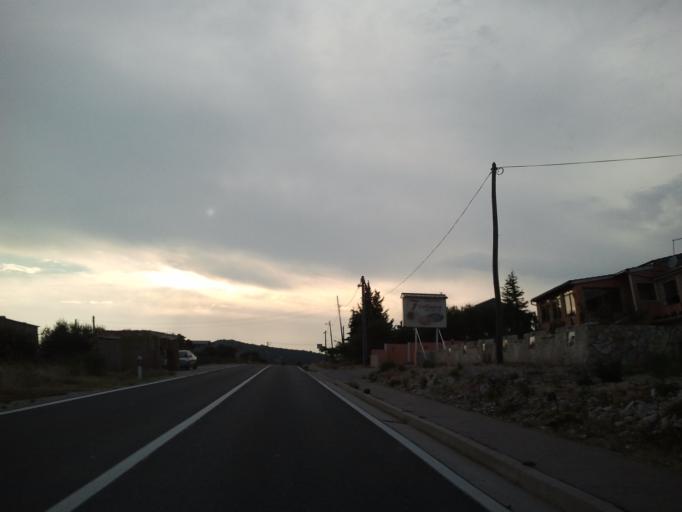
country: HR
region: Zadarska
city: Posedarje
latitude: 44.2205
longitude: 15.4522
